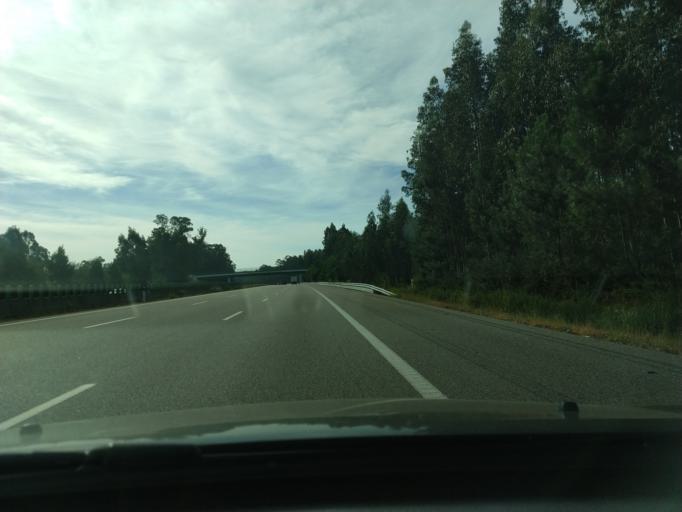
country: PT
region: Aveiro
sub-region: Ovar
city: Valega
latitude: 40.8709
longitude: -8.5602
